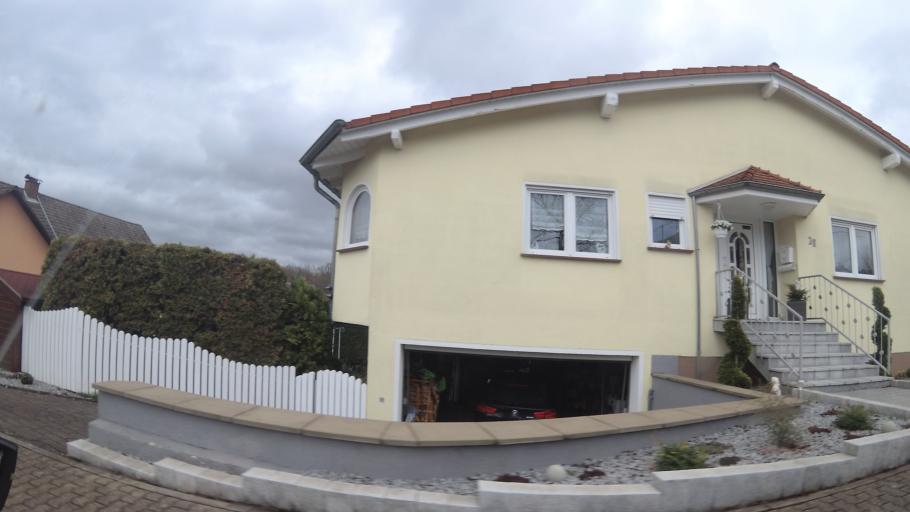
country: DE
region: Saarland
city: Ensdorf
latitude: 49.3074
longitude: 6.7863
